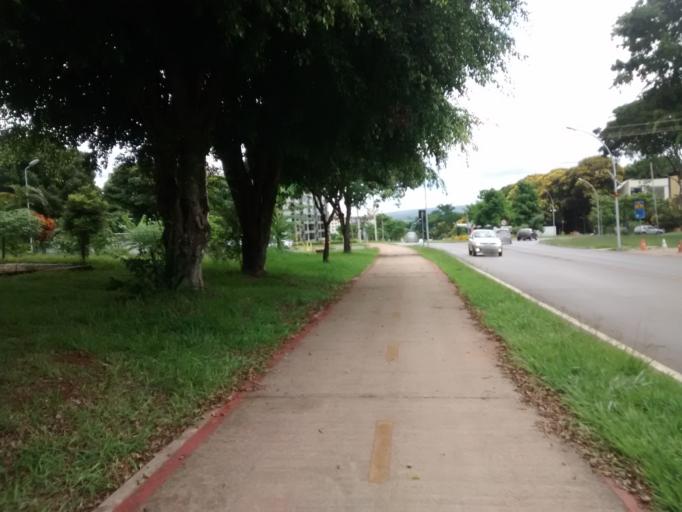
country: BR
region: Federal District
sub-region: Brasilia
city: Brasilia
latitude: -15.7550
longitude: -47.8829
